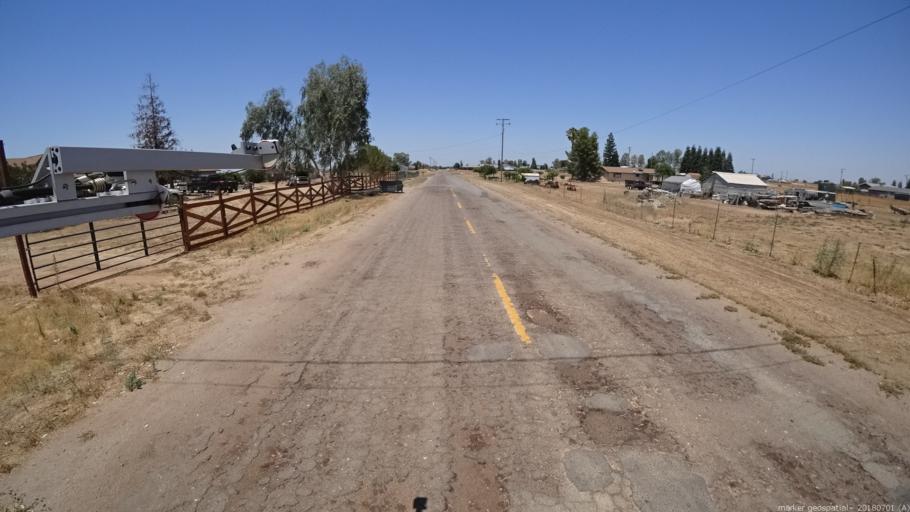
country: US
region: California
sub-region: Madera County
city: Madera Acres
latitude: 37.0336
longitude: -119.9942
